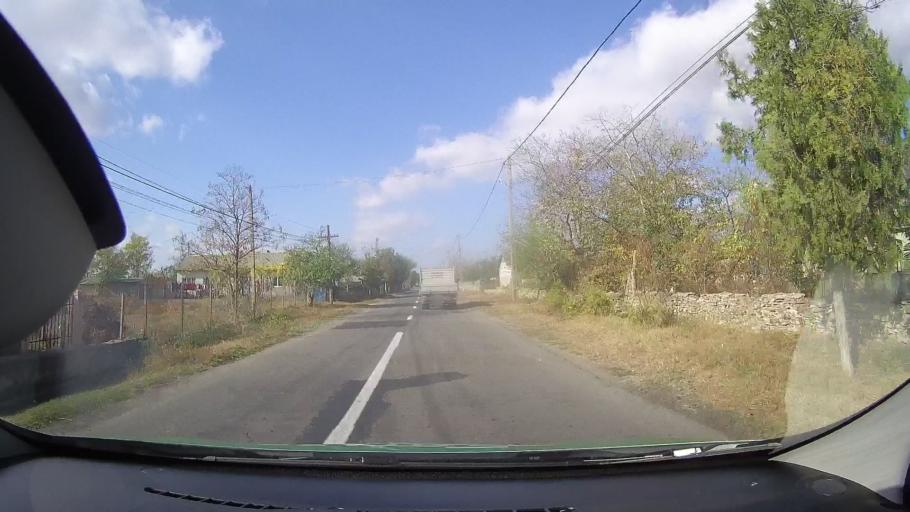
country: RO
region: Constanta
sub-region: Comuna Istria
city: Nuntasi
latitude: 44.5410
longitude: 28.6465
